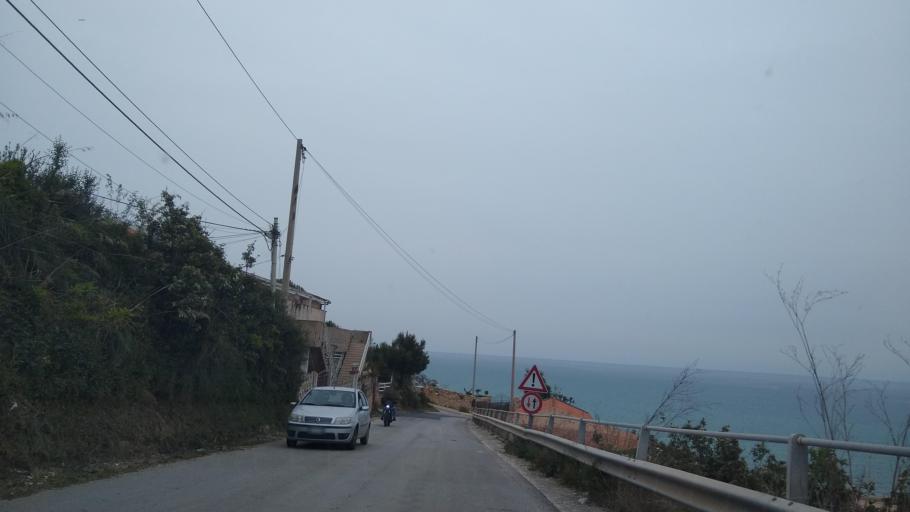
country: IT
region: Sicily
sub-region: Trapani
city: Castellammare del Golfo
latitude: 38.0213
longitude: 12.8972
